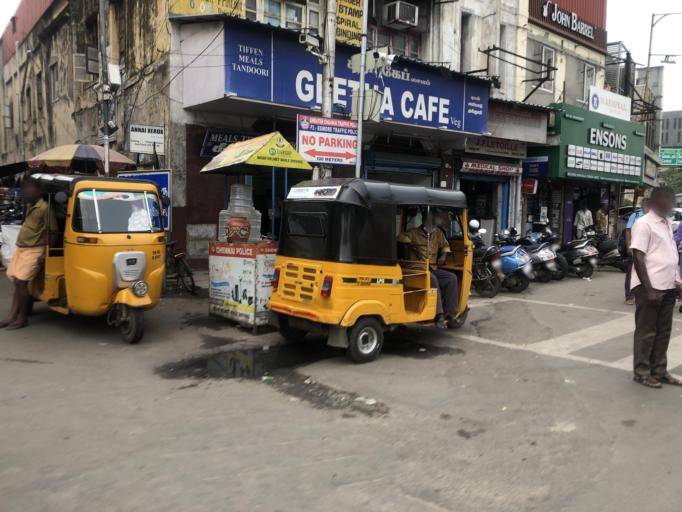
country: IN
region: Tamil Nadu
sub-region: Chennai
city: Chennai
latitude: 13.0682
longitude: 80.2709
